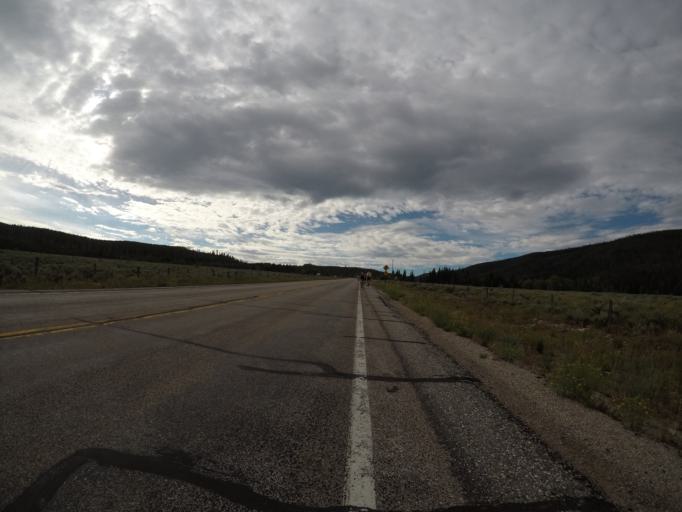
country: US
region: Wyoming
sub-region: Carbon County
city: Saratoga
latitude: 41.3484
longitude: -106.5298
